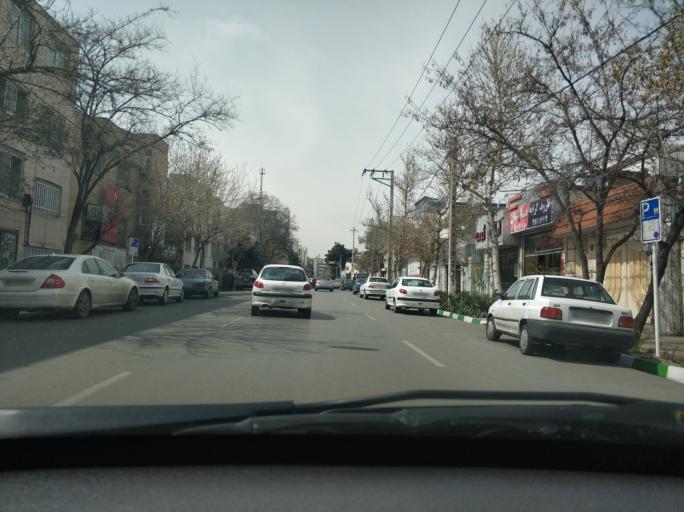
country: IR
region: Razavi Khorasan
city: Mashhad
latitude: 36.3054
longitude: 59.5673
